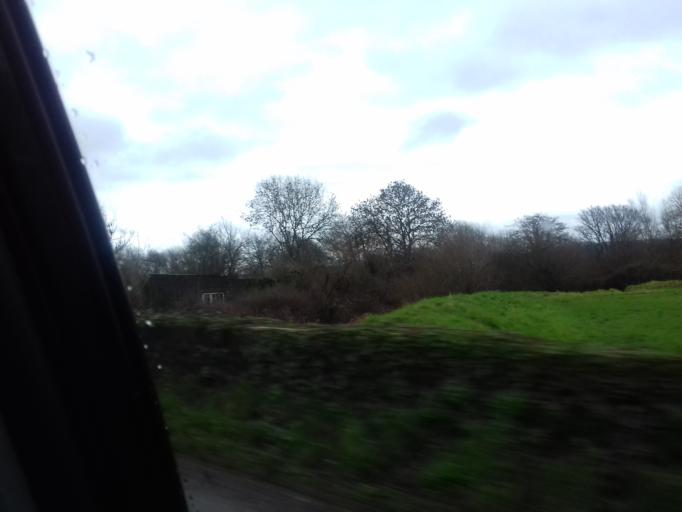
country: IE
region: Leinster
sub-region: County Carlow
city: Bagenalstown
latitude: 52.6471
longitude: -6.9885
